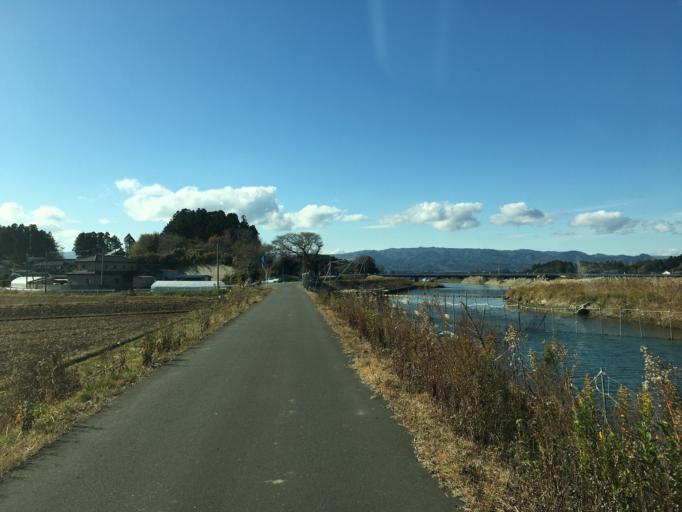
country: JP
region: Miyagi
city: Marumori
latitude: 37.8081
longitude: 140.9620
